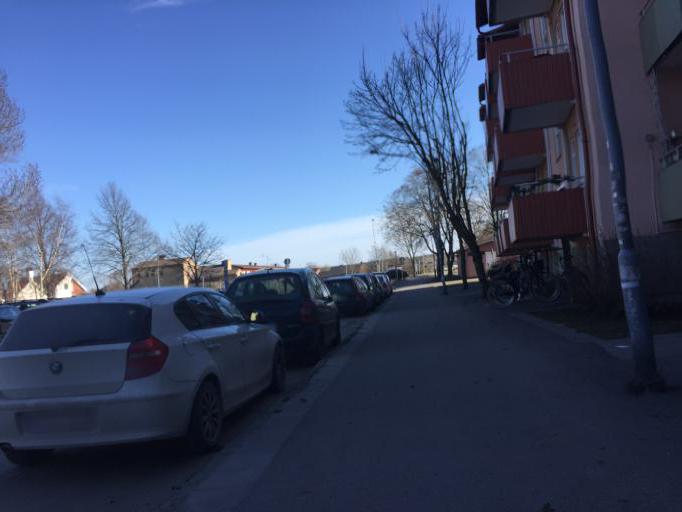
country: SE
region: OErebro
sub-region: Orebro Kommun
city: Orebro
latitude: 59.2641
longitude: 15.2083
